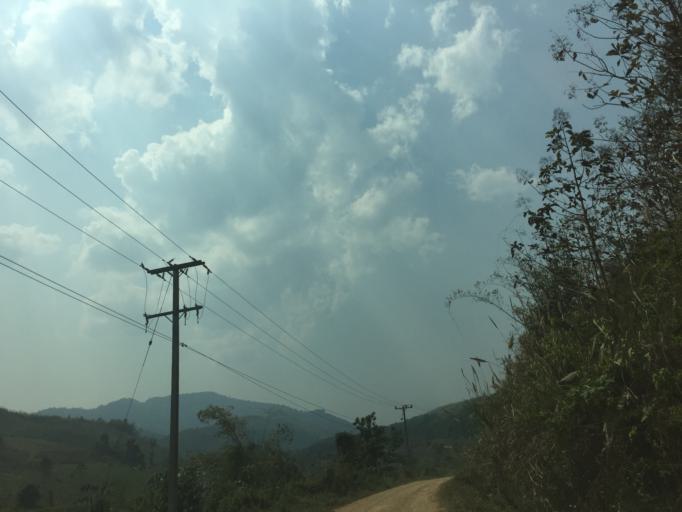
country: TH
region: Nan
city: Thung Chang
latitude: 19.7294
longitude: 100.7429
